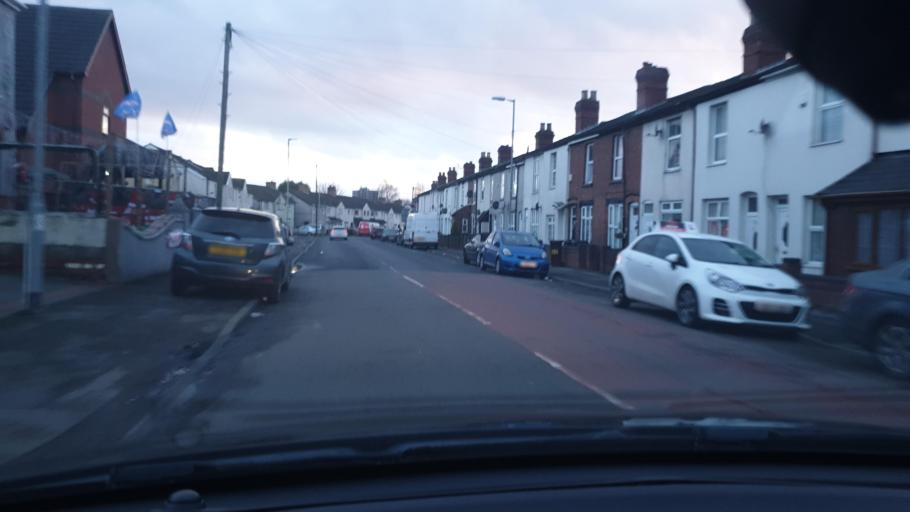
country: GB
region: England
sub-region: Wolverhampton
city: Wolverhampton
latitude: 52.6003
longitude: -2.1364
